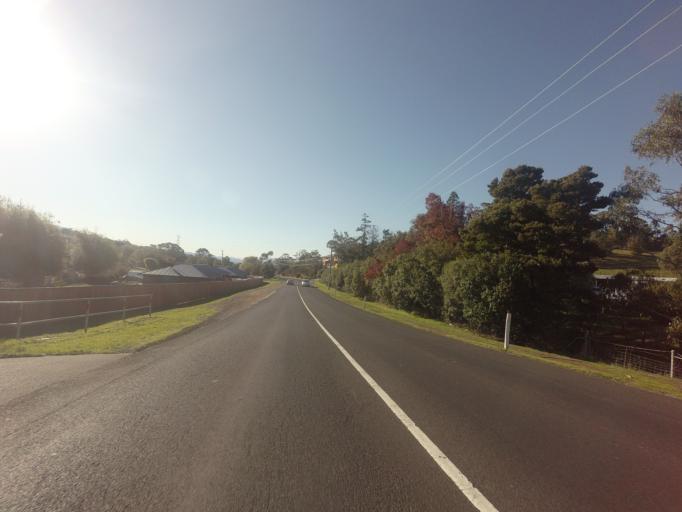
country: AU
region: Tasmania
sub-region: Glenorchy
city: West Moonah
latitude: -42.8540
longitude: 147.2682
